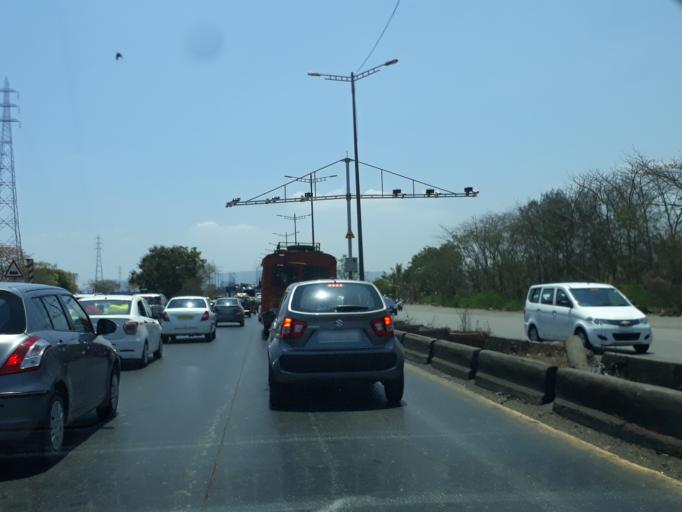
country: IN
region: Maharashtra
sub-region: Thane
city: Navi Mumbai
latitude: 19.0587
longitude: 72.9580
